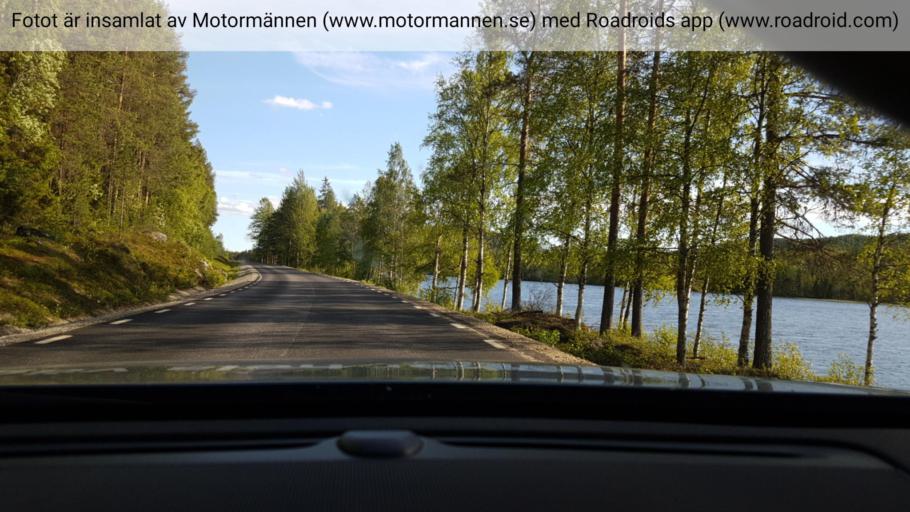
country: SE
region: Vaesterbotten
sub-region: Vindelns Kommun
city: Vindeln
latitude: 64.4460
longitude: 19.3391
